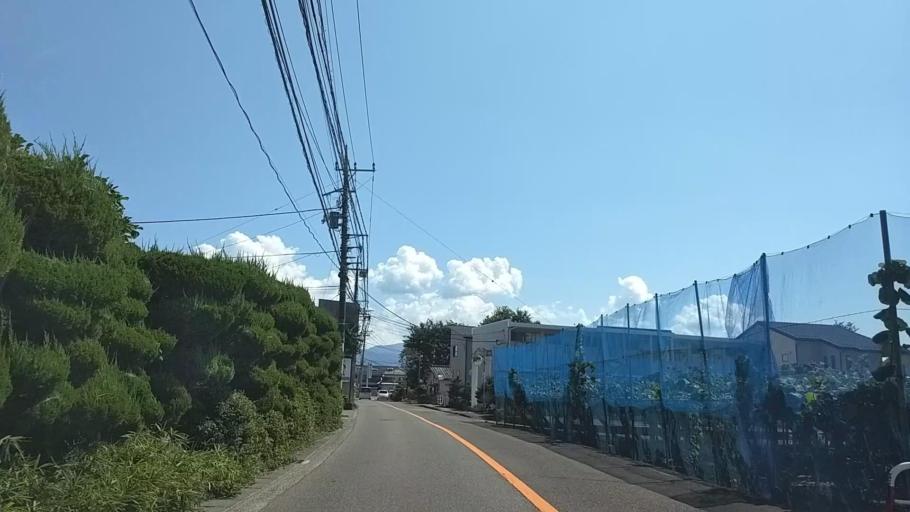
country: JP
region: Yamanashi
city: Ryuo
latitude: 35.6484
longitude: 138.5169
